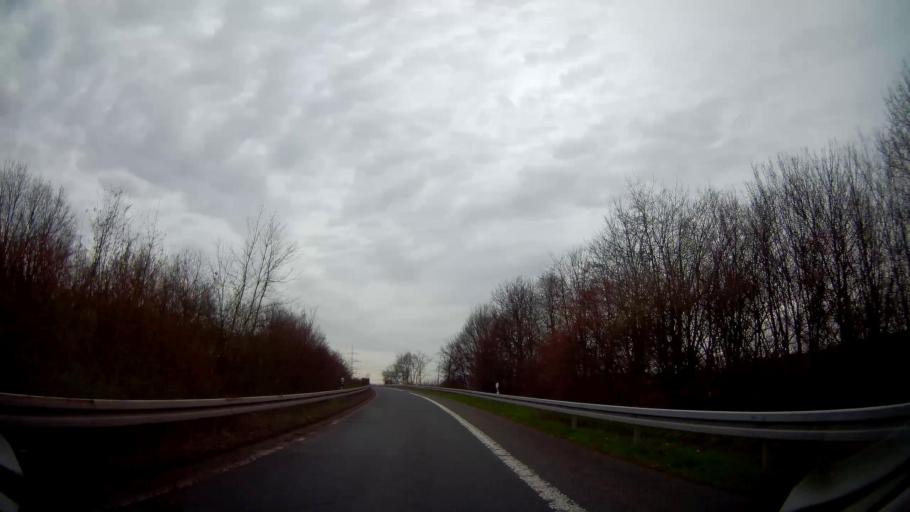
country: DE
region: North Rhine-Westphalia
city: Marl
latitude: 51.6402
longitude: 7.0312
